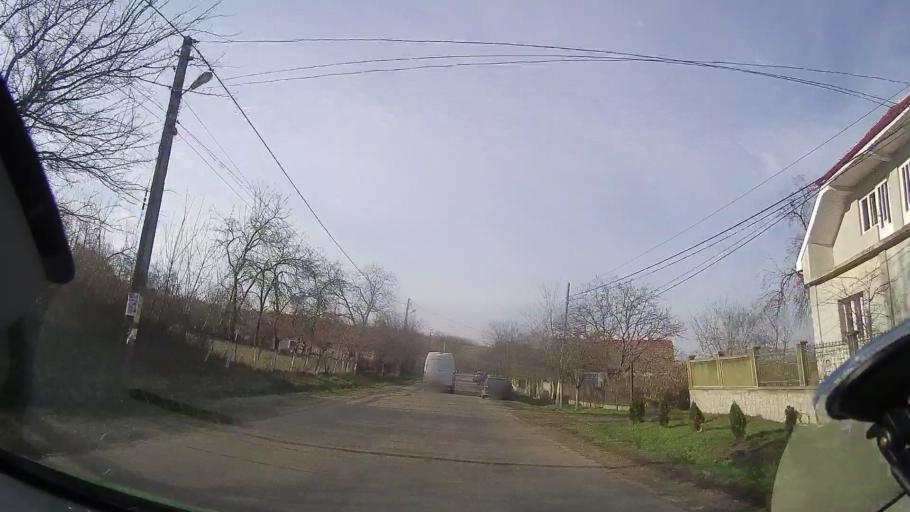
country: RO
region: Bihor
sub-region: Comuna Spinus
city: Spinus
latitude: 47.2011
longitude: 22.1853
